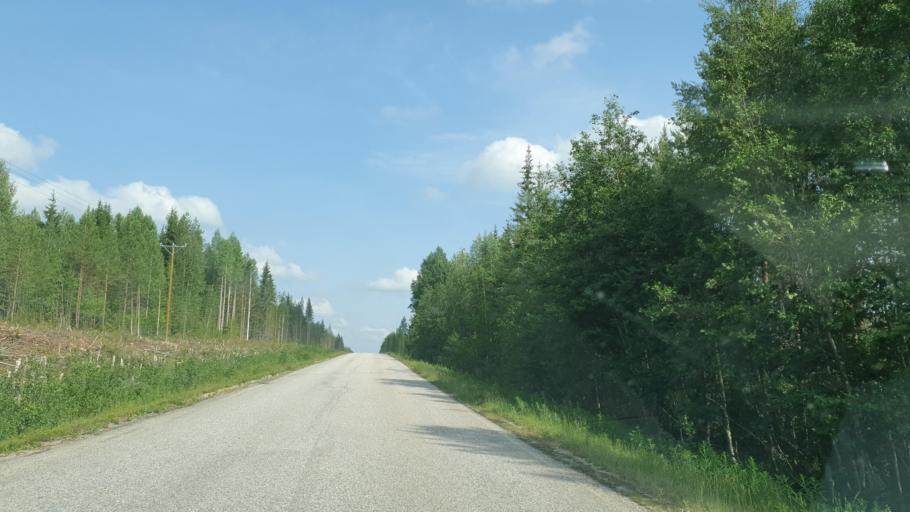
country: FI
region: Kainuu
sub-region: Kehys-Kainuu
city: Kuhmo
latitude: 64.0383
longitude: 29.9317
